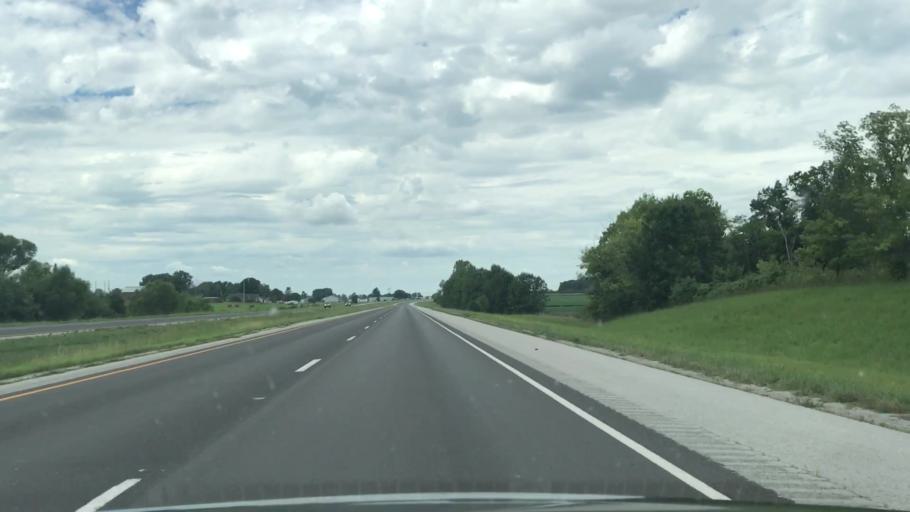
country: US
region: Kentucky
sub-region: Todd County
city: Elkton
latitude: 36.8038
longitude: -87.0816
